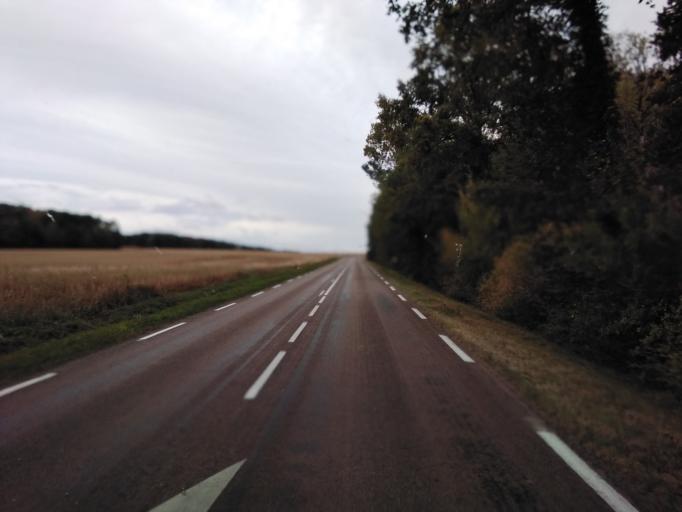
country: FR
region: Champagne-Ardenne
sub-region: Departement de l'Aube
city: Vendeuvre-sur-Barse
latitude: 48.2075
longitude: 4.4459
